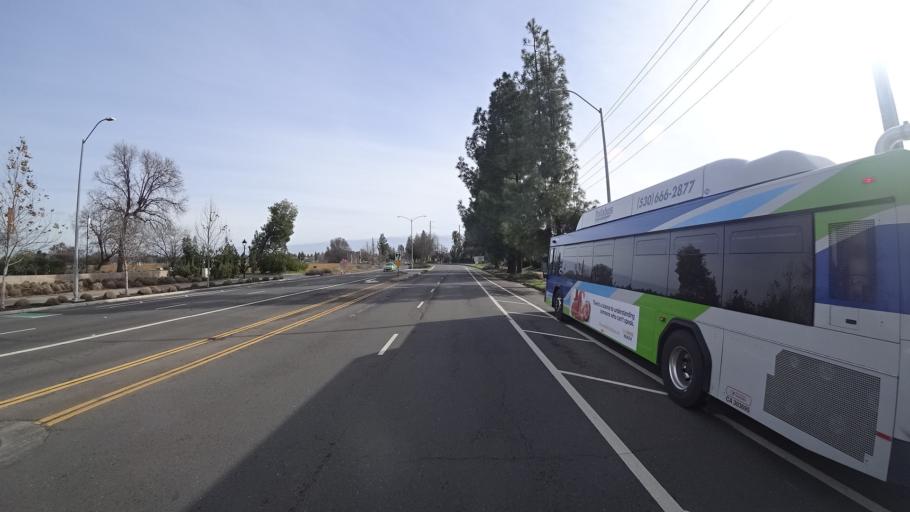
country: US
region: California
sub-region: Yolo County
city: Davis
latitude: 38.5607
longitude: -121.7383
